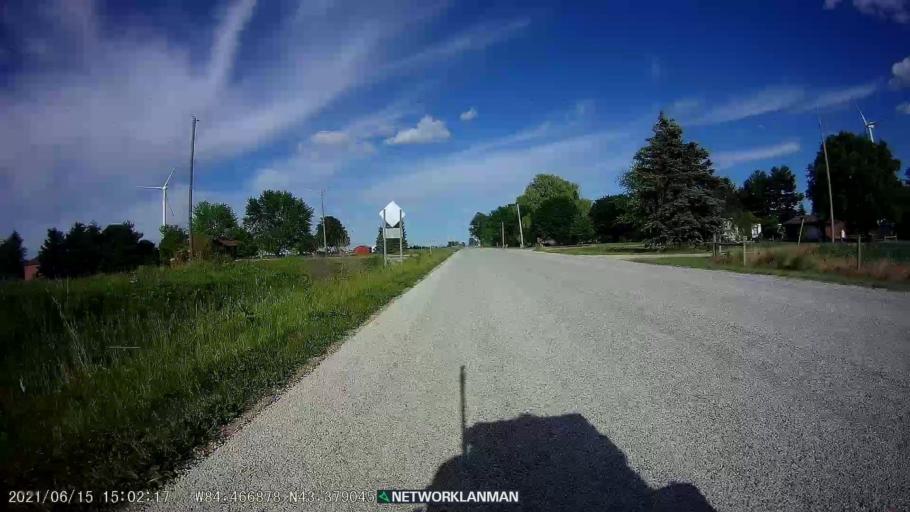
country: US
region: Michigan
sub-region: Gratiot County
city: Breckenridge
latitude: 43.3790
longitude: -84.4671
